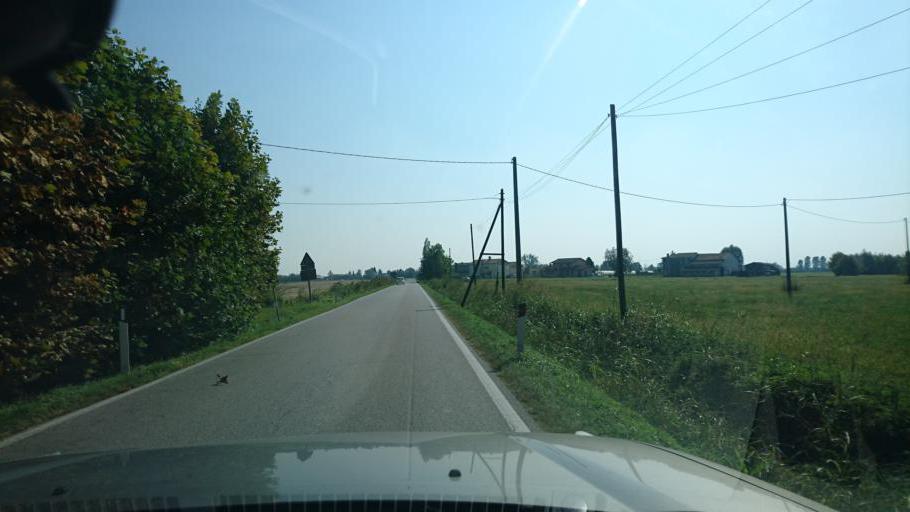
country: IT
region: Veneto
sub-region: Provincia di Vicenza
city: Camisano Vicentino
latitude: 45.5474
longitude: 11.7131
